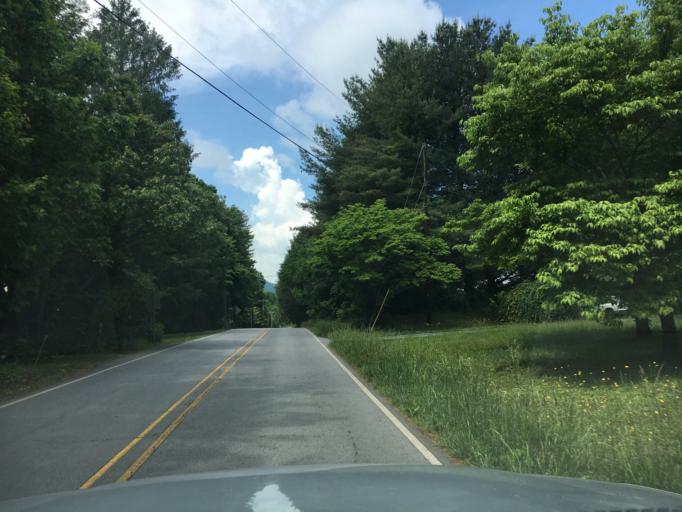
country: US
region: North Carolina
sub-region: Henderson County
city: Mills River
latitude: 35.3766
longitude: -82.5754
